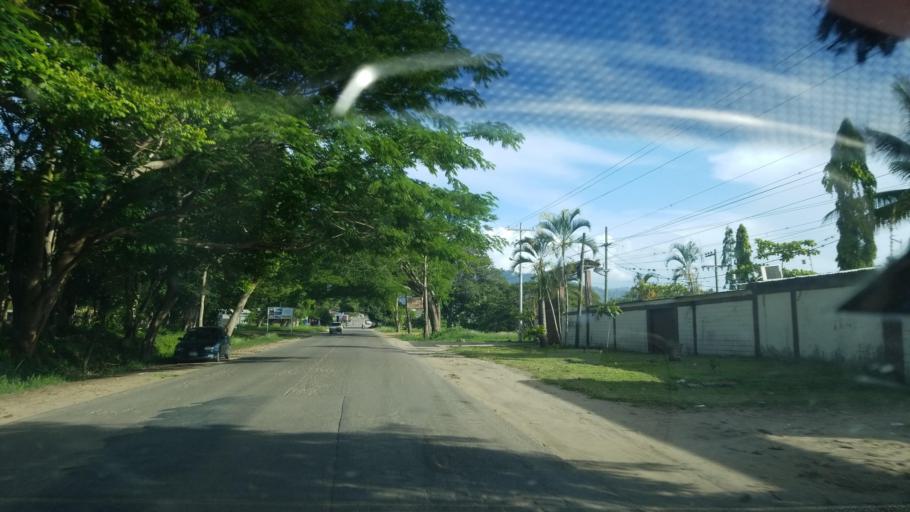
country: HN
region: El Paraiso
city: Cuyali
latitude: 13.8898
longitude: -86.5550
